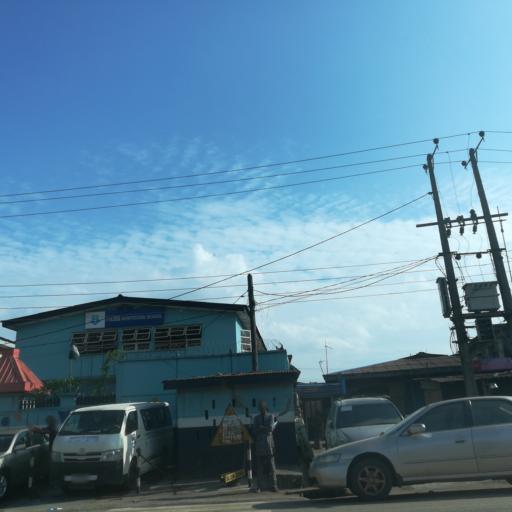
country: NG
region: Lagos
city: Agege
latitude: 6.6145
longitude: 3.3269
